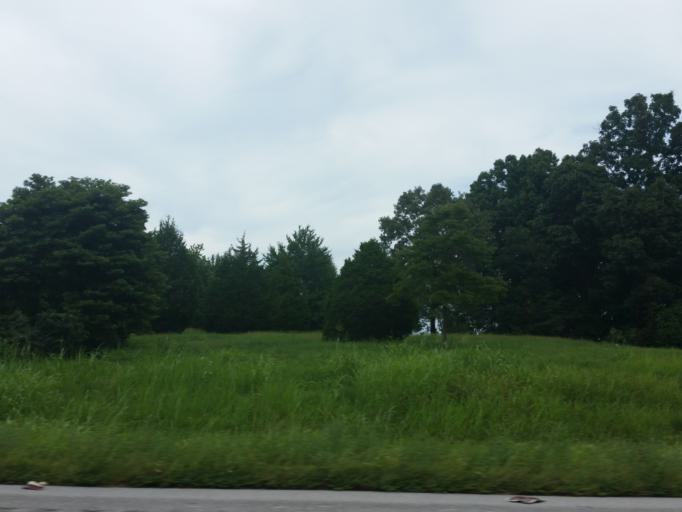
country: US
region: Kentucky
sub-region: Trigg County
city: Cadiz
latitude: 36.9450
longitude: -87.8374
